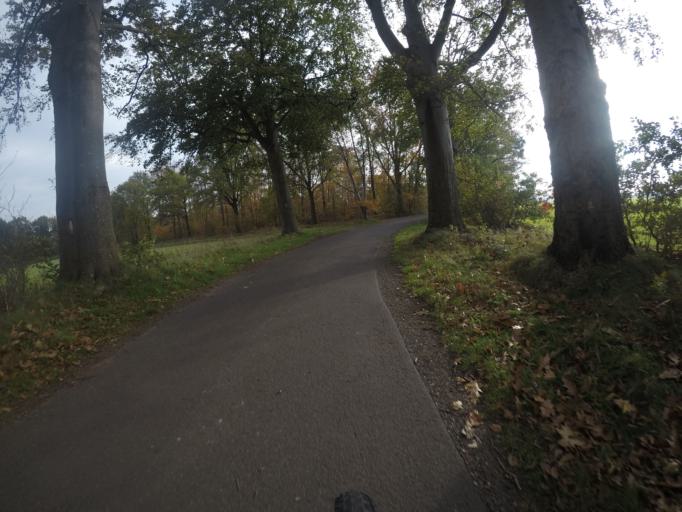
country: DE
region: North Rhine-Westphalia
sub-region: Regierungsbezirk Munster
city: Isselburg
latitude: 51.8399
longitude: 6.4873
